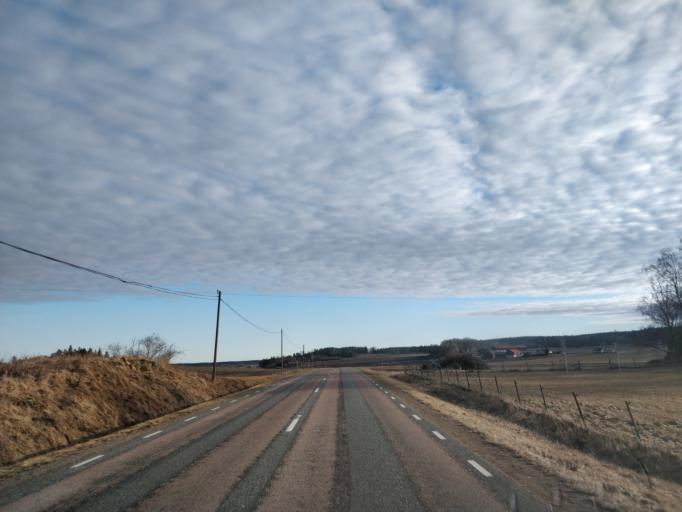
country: SE
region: Uppsala
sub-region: Enkopings Kommun
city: Enkoping
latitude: 59.7725
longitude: 17.0841
